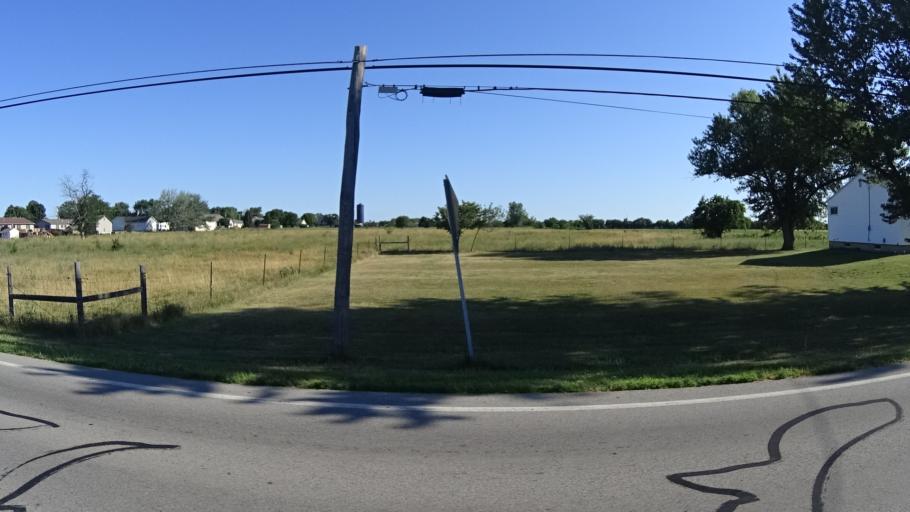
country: US
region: Ohio
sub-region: Erie County
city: Sandusky
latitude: 41.3979
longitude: -82.7693
